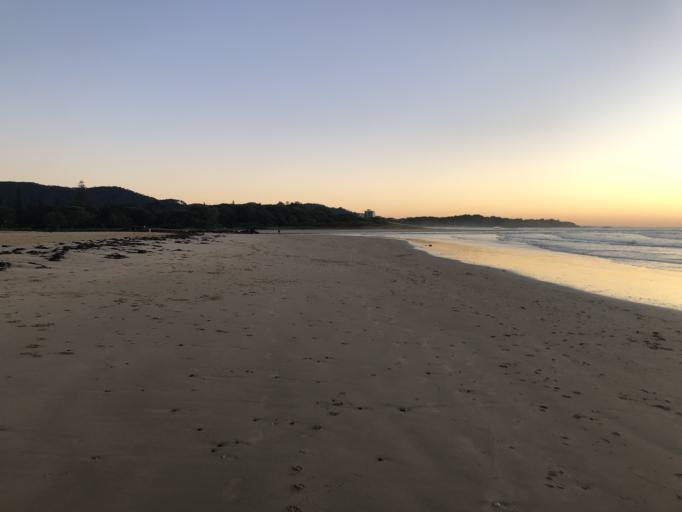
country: AU
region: New South Wales
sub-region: Coffs Harbour
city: Coffs Harbour
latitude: -30.2983
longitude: 153.1398
